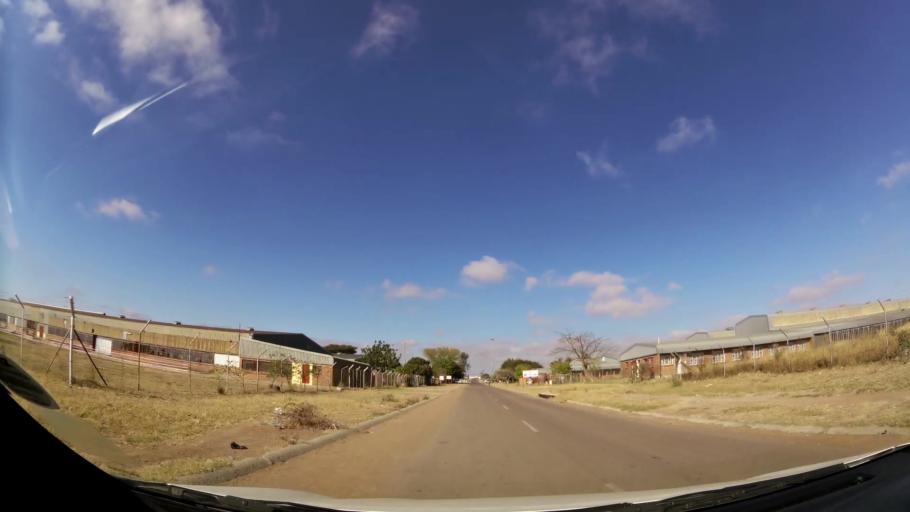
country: ZA
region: Limpopo
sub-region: Capricorn District Municipality
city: Polokwane
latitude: -23.8434
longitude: 29.4008
